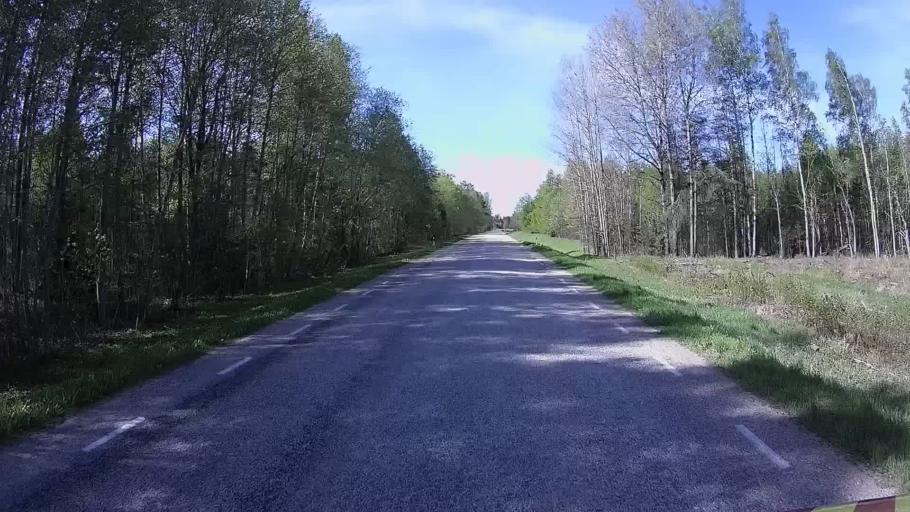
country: EE
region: Polvamaa
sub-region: Raepina vald
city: Rapina
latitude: 57.9715
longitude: 27.5575
